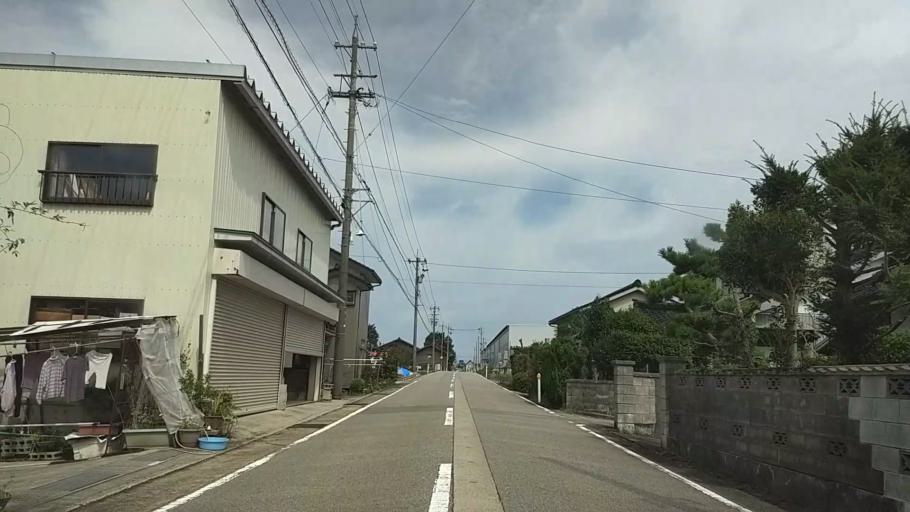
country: JP
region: Toyama
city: Kamiichi
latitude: 36.7427
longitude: 137.3735
